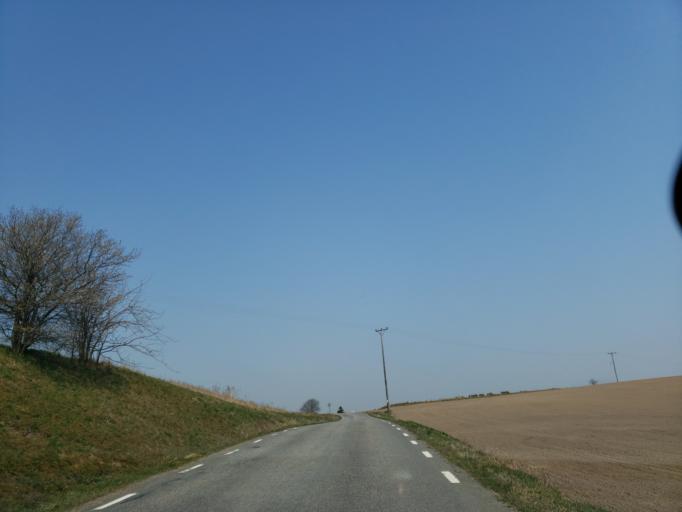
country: SE
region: Skane
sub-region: Simrishamns Kommun
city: Simrishamn
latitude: 55.4781
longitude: 14.2313
